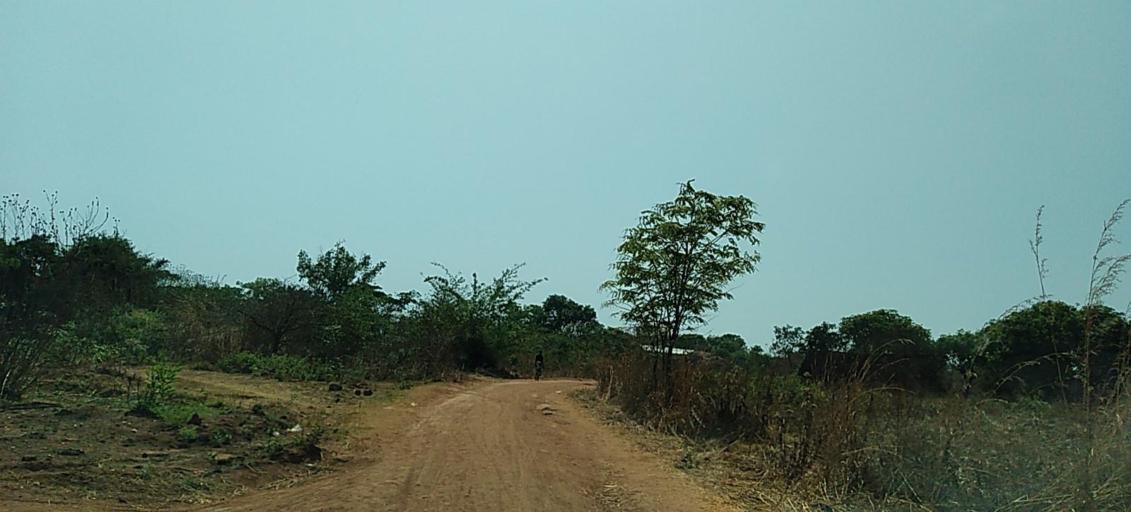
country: ZM
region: Copperbelt
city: Luanshya
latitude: -13.3486
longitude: 28.3997
